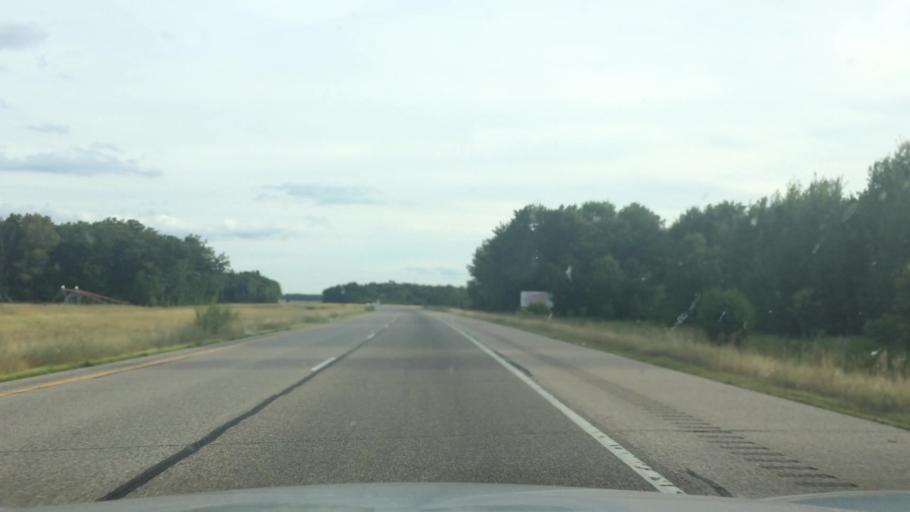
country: US
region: Wisconsin
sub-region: Waushara County
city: Wautoma
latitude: 44.1743
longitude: -89.5312
